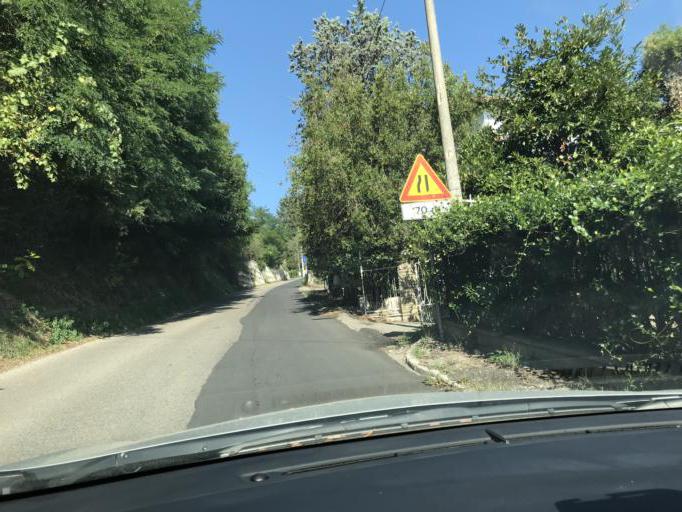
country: IT
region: Umbria
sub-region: Provincia di Perugia
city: Ponte Felcino
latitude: 43.1076
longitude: 12.4430
